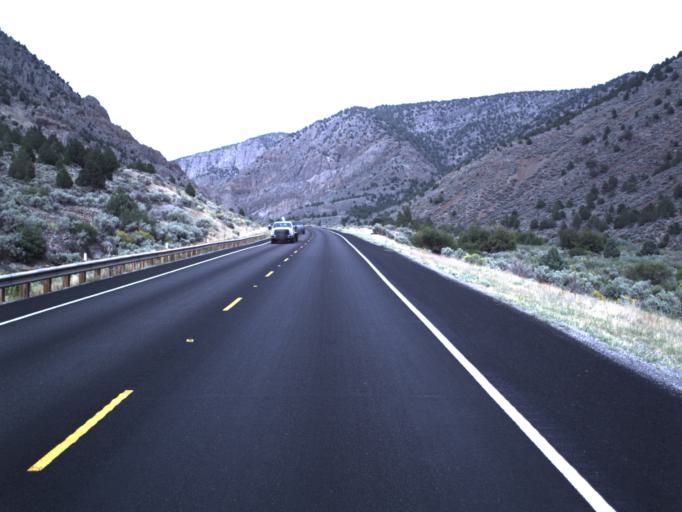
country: US
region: Utah
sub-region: Piute County
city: Junction
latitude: 38.0884
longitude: -112.3390
